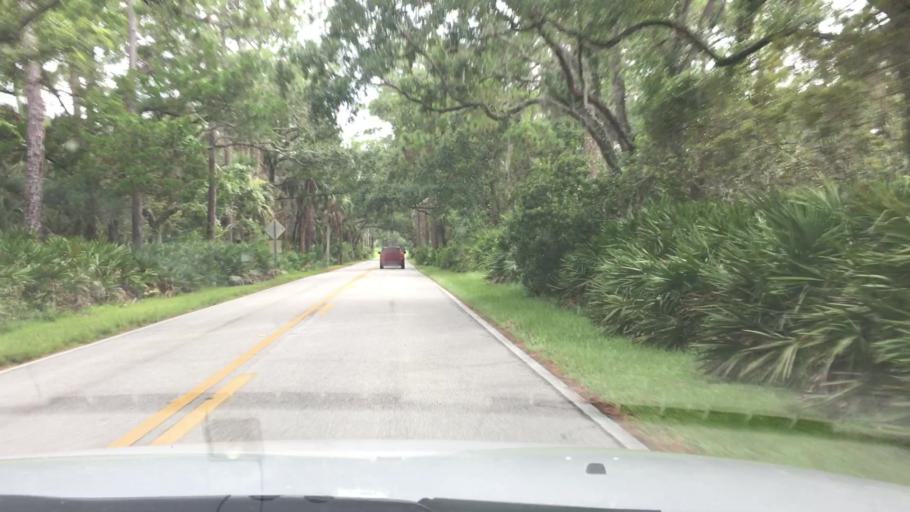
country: US
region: Florida
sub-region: Volusia County
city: Ormond-by-the-Sea
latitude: 29.3444
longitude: -81.0951
